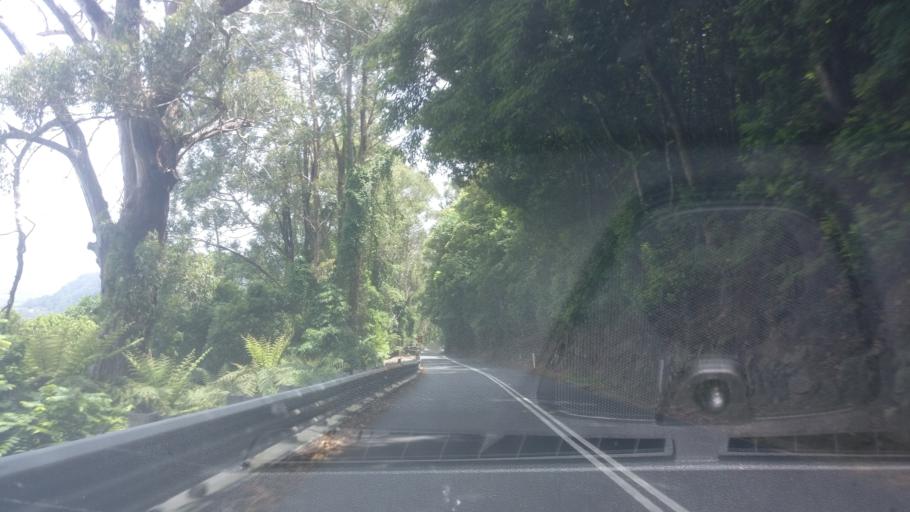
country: AU
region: New South Wales
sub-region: Shoalhaven Shire
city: Kangaroo Valley
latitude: -34.7901
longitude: 150.5625
